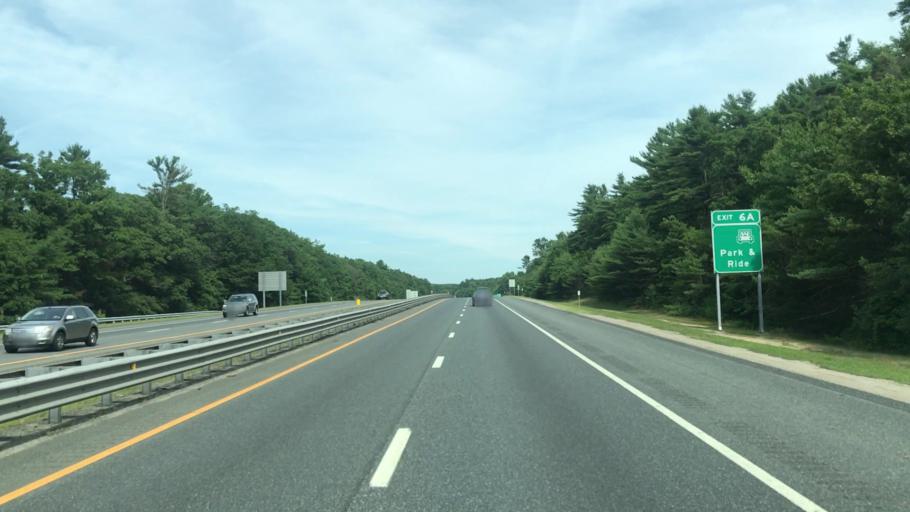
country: US
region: Rhode Island
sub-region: Kent County
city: West Greenwich
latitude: 41.6502
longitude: -71.5978
